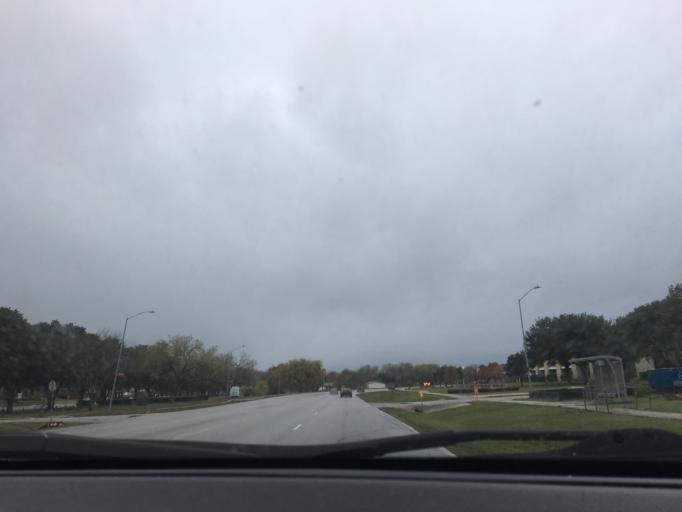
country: US
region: Texas
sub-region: Hays County
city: San Marcos
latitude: 29.8857
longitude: -97.9300
